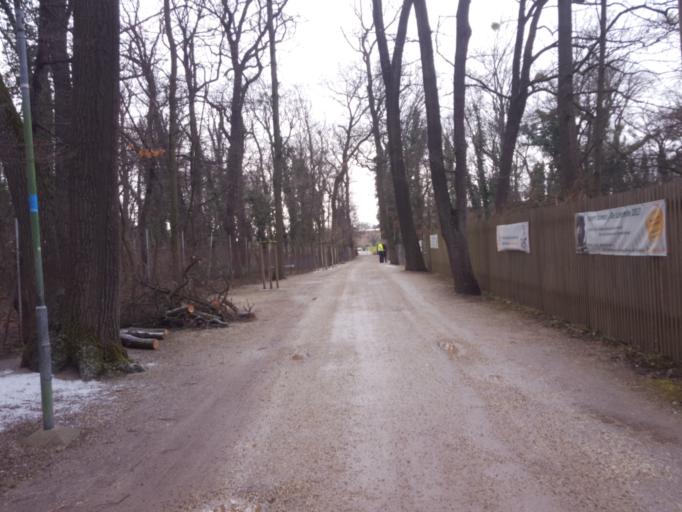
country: AT
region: Lower Austria
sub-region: Politischer Bezirk Modling
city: Vosendorf
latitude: 48.1783
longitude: 16.3037
